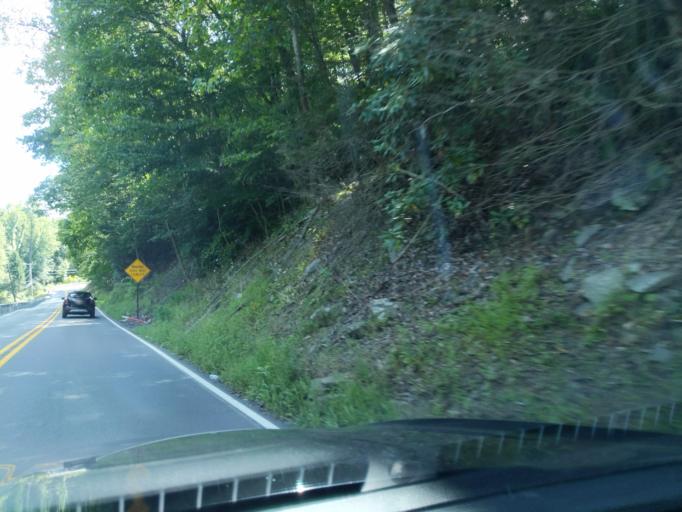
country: US
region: Pennsylvania
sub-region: Blair County
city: Greenwood
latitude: 40.5285
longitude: -78.2989
